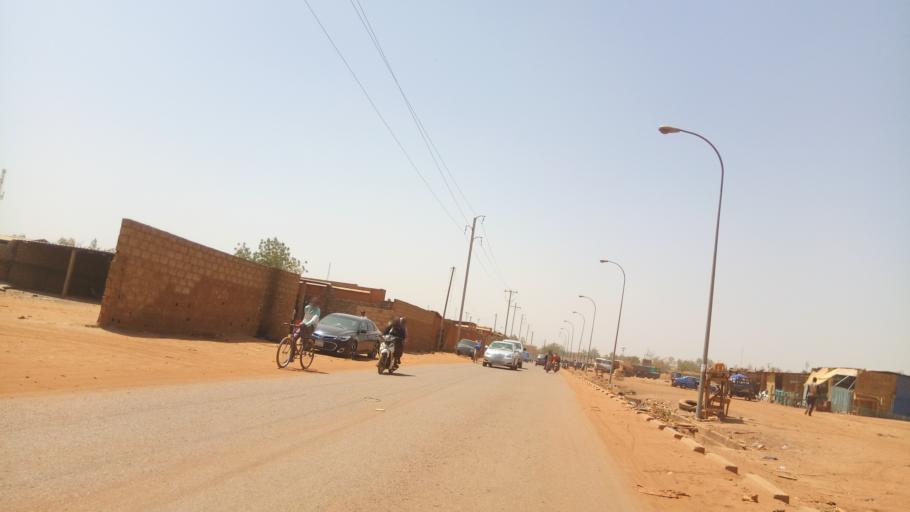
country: BF
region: Centre
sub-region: Kadiogo Province
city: Ouagadougou
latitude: 12.3949
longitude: -1.5653
